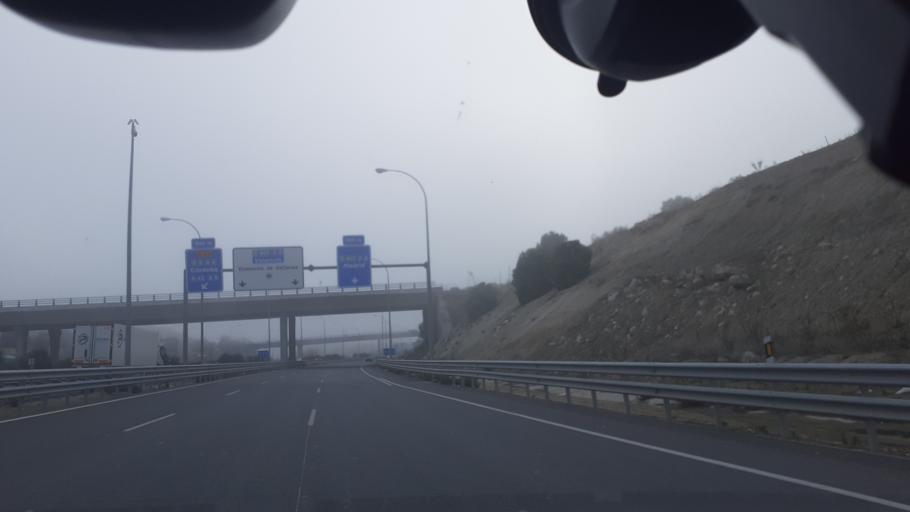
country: ES
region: Madrid
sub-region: Provincia de Madrid
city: Villa de Vallecas
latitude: 40.3790
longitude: -3.5910
